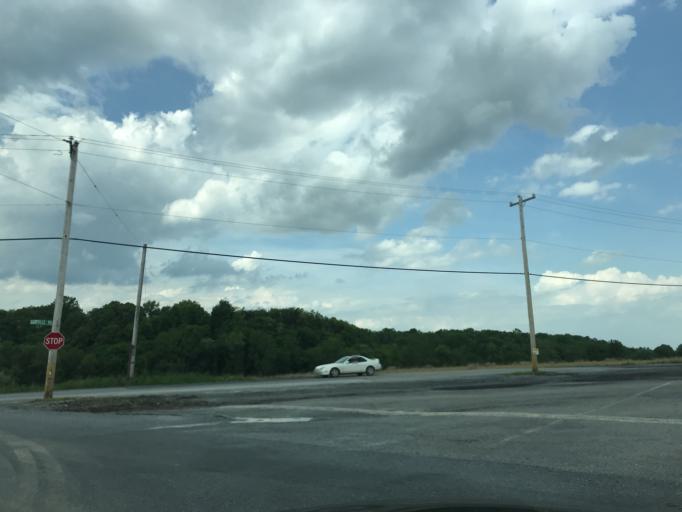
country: US
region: Pennsylvania
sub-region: York County
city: Susquehanna Trails
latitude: 39.7296
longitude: -76.3045
